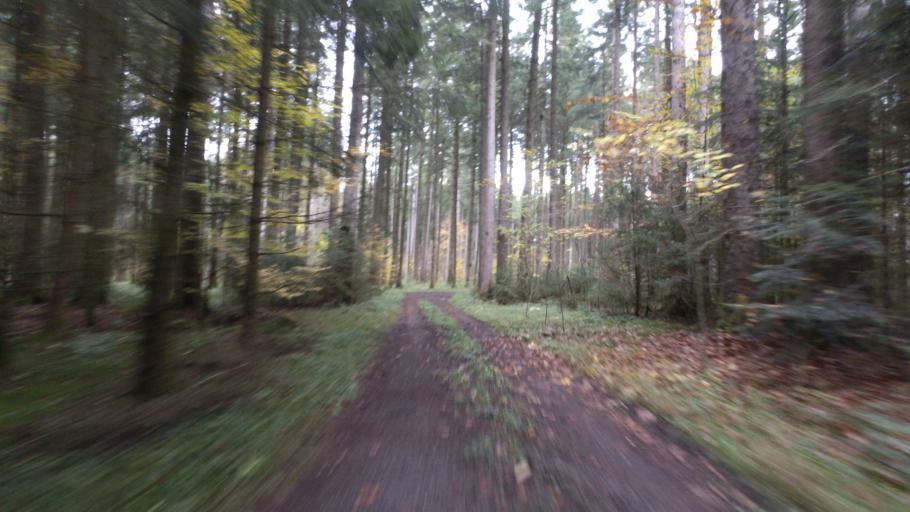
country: DE
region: Bavaria
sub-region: Upper Bavaria
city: Nussdorf
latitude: 47.9097
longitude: 12.5774
